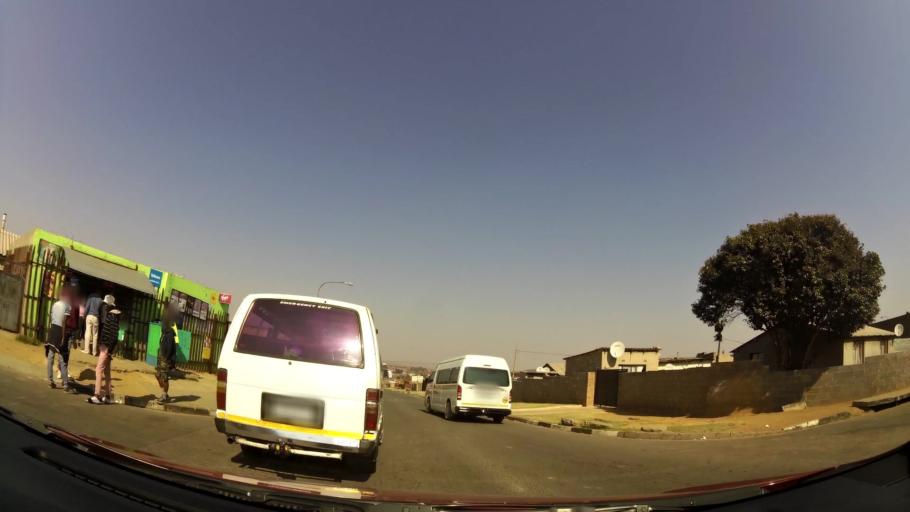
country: ZA
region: Gauteng
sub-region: City of Johannesburg Metropolitan Municipality
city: Soweto
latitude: -26.2453
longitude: 27.9379
